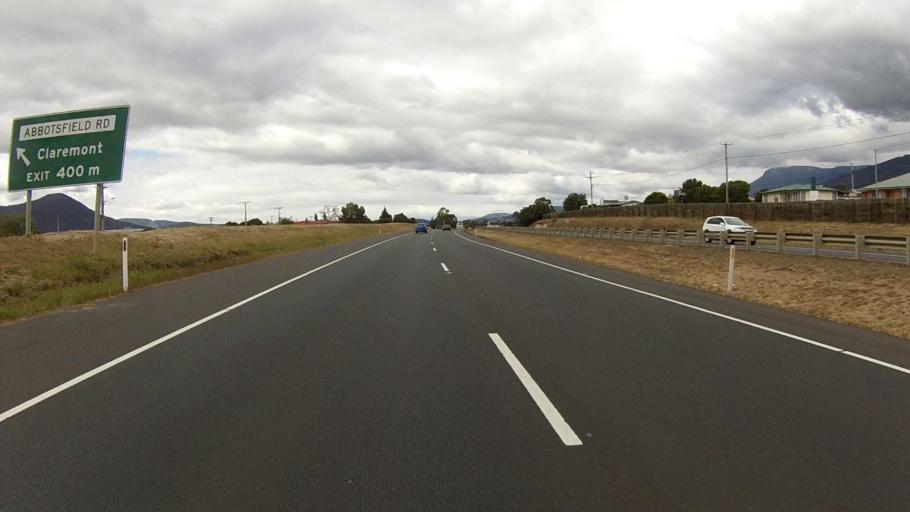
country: AU
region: Tasmania
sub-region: Glenorchy
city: Claremont
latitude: -42.7849
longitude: 147.2418
